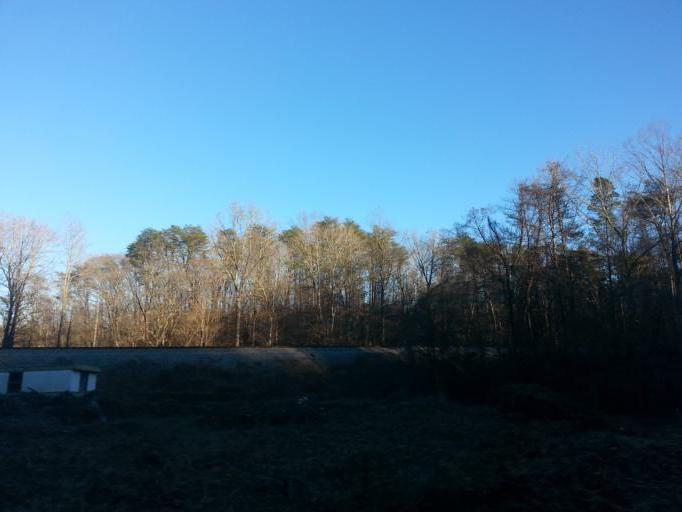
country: US
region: Tennessee
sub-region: Anderson County
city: Rocky Top
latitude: 36.2044
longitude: -84.1484
